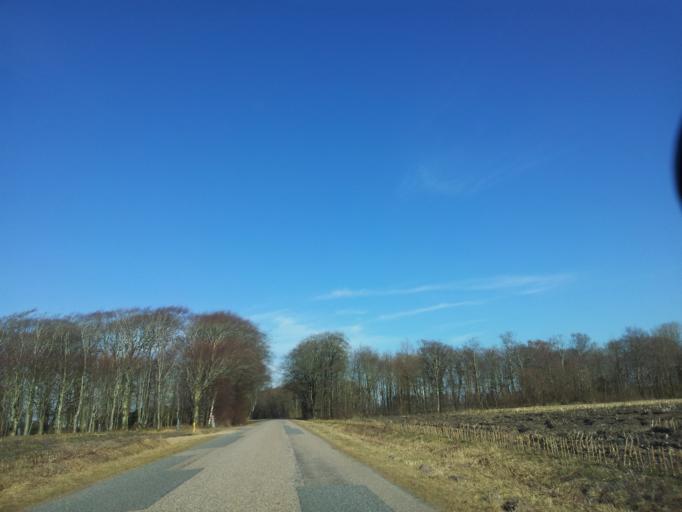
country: DK
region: South Denmark
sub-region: Tonder Kommune
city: Sherrebek
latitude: 55.2005
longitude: 8.7438
